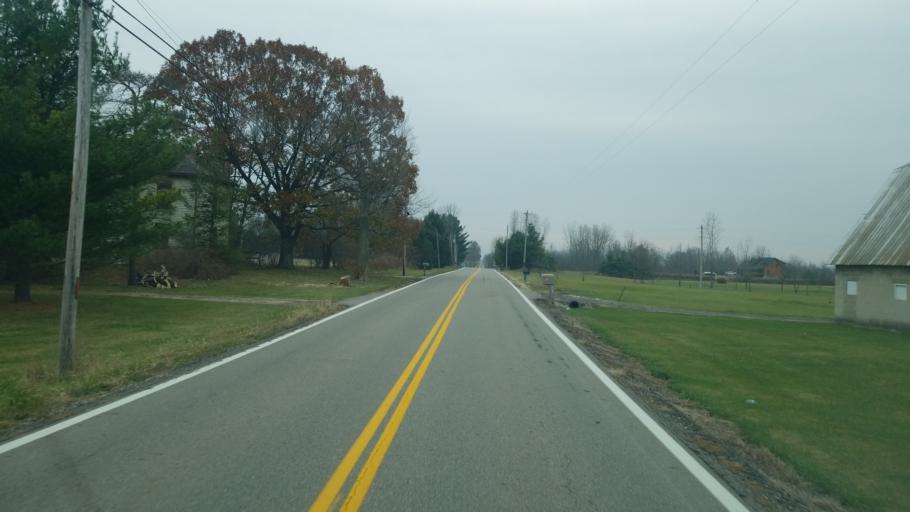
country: US
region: Ohio
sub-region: Knox County
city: Centerburg
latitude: 40.2894
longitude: -82.6301
